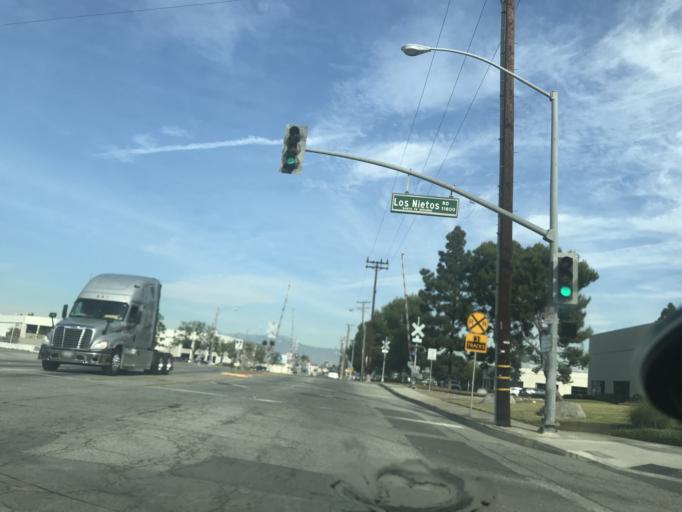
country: US
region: California
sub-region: Los Angeles County
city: Santa Fe Springs
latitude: 33.9575
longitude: -118.0713
